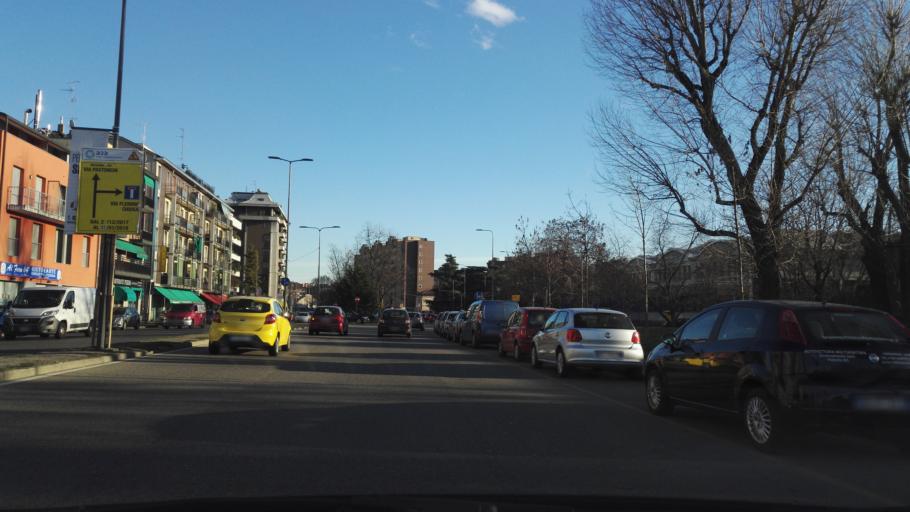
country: IT
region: Lombardy
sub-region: Citta metropolitana di Milano
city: Romano Banco
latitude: 45.4711
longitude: 9.1219
